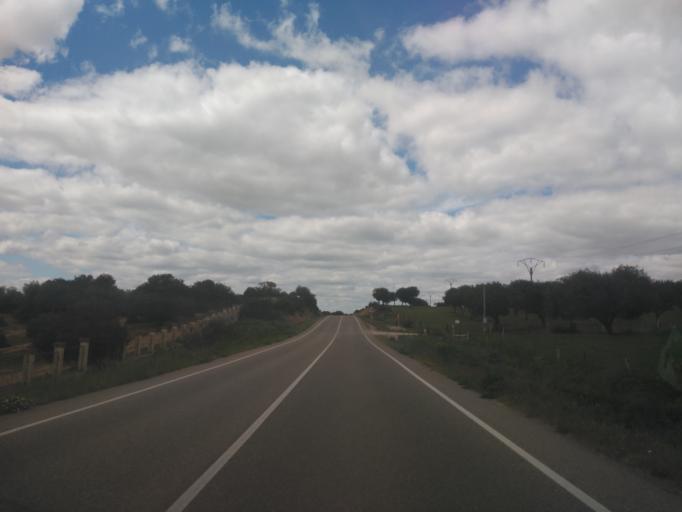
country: ES
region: Castille and Leon
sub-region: Provincia de Salamanca
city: Florida de Liebana
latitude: 41.0378
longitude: -5.7397
